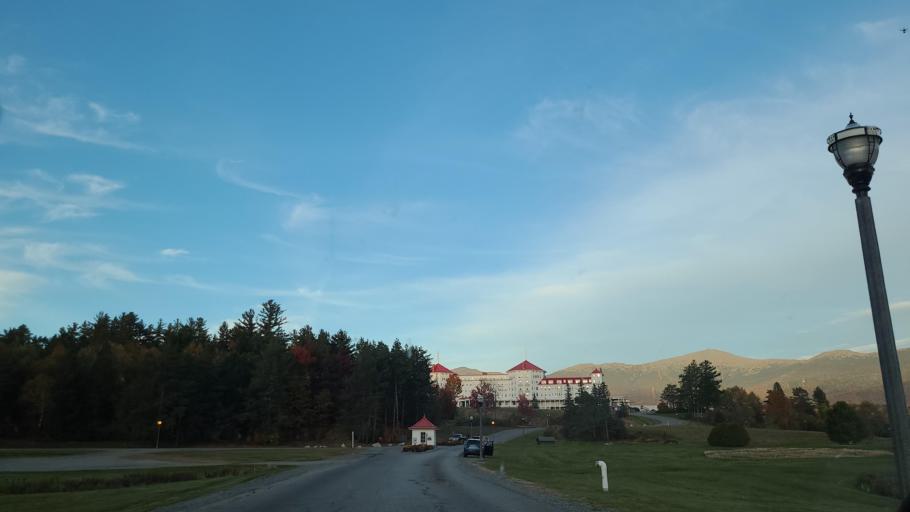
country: US
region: New Hampshire
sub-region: Coos County
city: Jefferson
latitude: 44.2556
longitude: -71.4446
